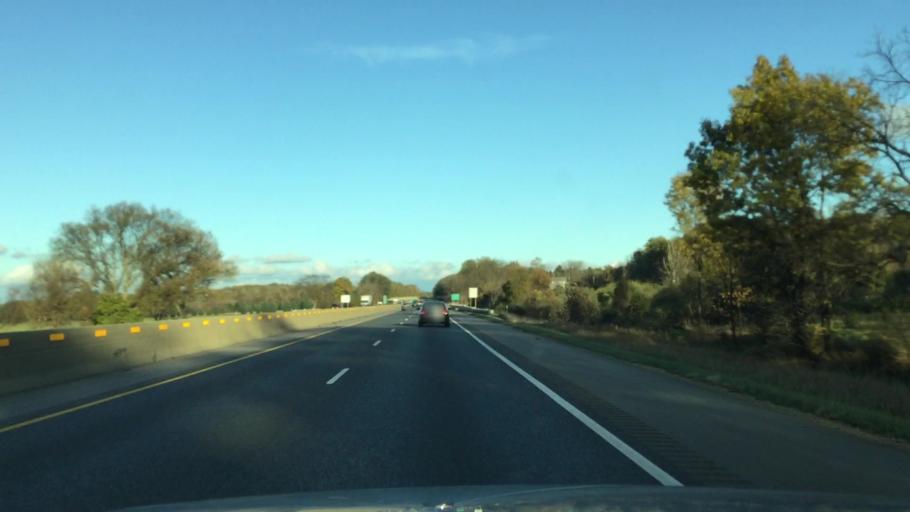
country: US
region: Michigan
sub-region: Kalamazoo County
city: Galesburg
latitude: 42.2769
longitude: -85.4100
